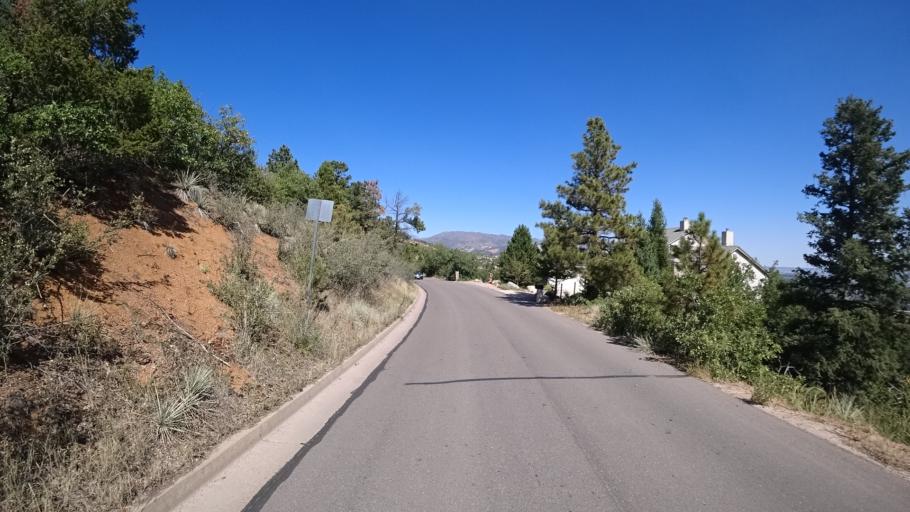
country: US
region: Colorado
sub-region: El Paso County
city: Manitou Springs
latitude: 38.8177
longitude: -104.8820
